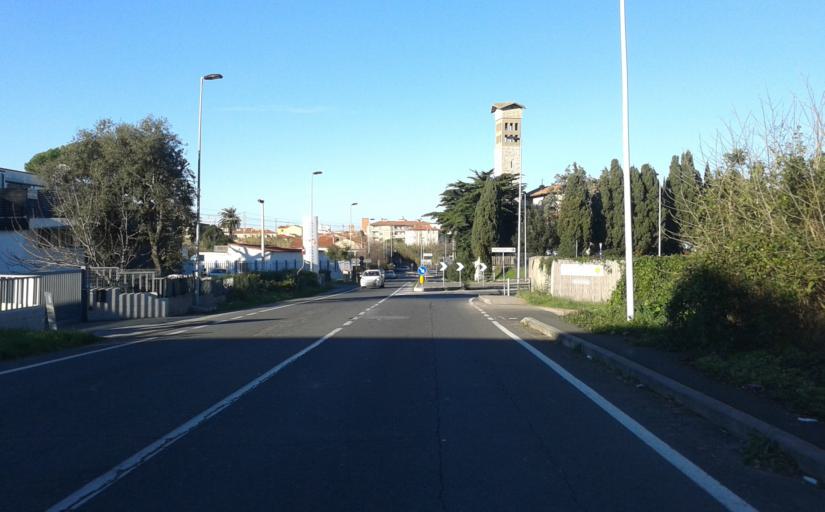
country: IT
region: Tuscany
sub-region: Provincia di Livorno
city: Livorno
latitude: 43.5115
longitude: 10.3268
